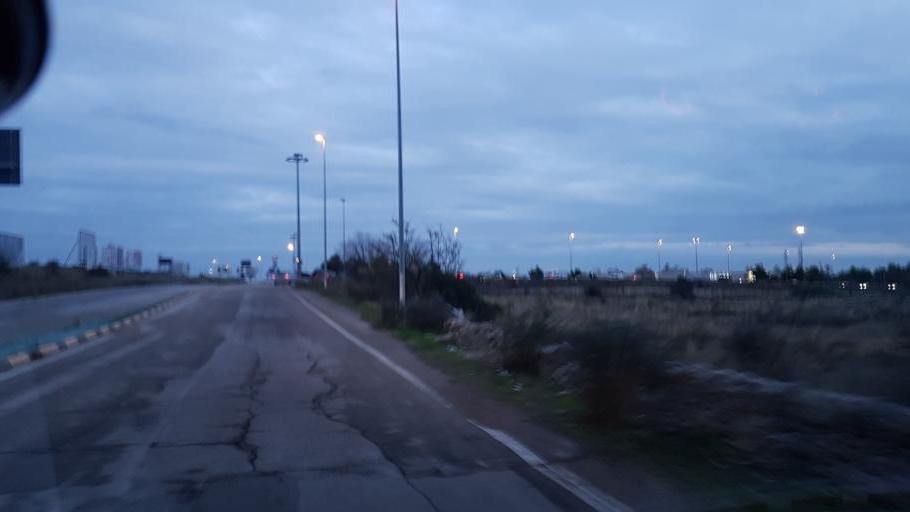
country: IT
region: Apulia
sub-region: Provincia di Taranto
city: Paolo VI
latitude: 40.5190
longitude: 17.2859
